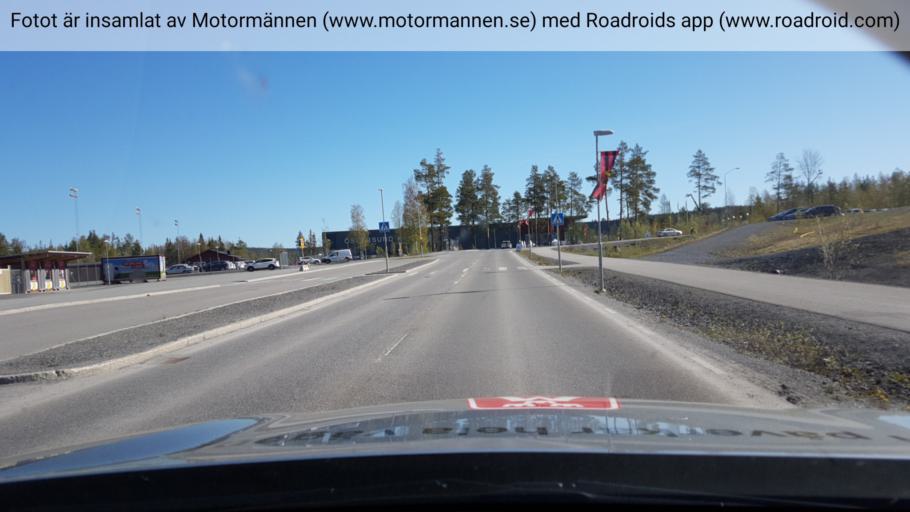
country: SE
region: Jaemtland
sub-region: OEstersunds Kommun
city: Ostersund
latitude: 63.1940
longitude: 14.6568
